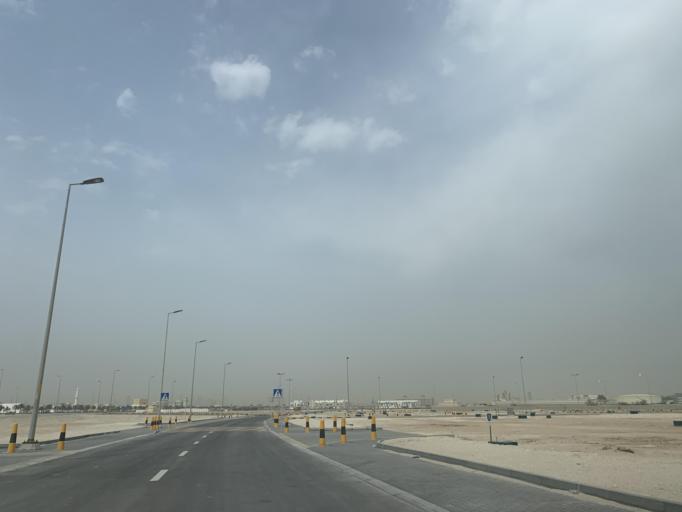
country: BH
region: Northern
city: Madinat `Isa
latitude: 26.1835
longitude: 50.5070
